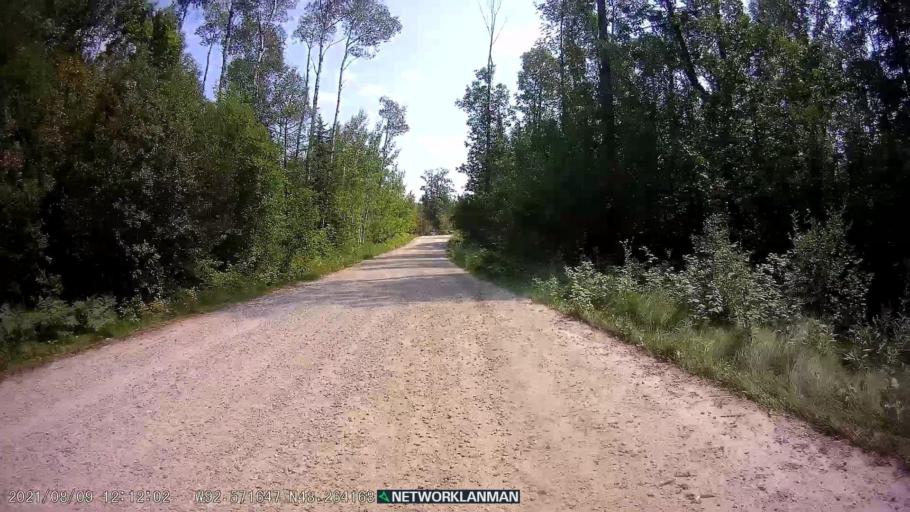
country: US
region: Minnesota
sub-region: Saint Louis County
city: Parkville
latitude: 48.2643
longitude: -92.5719
